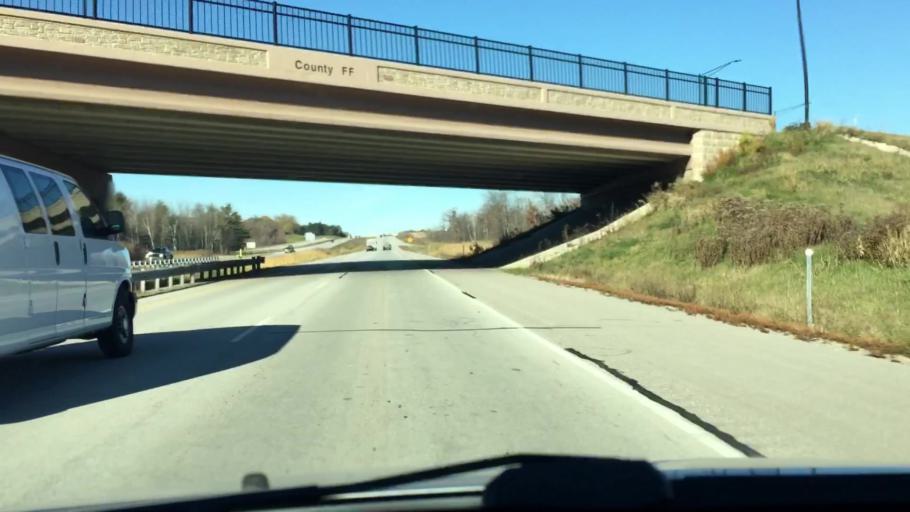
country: US
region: Wisconsin
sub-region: Brown County
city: Howard
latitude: 44.5605
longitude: -88.1301
